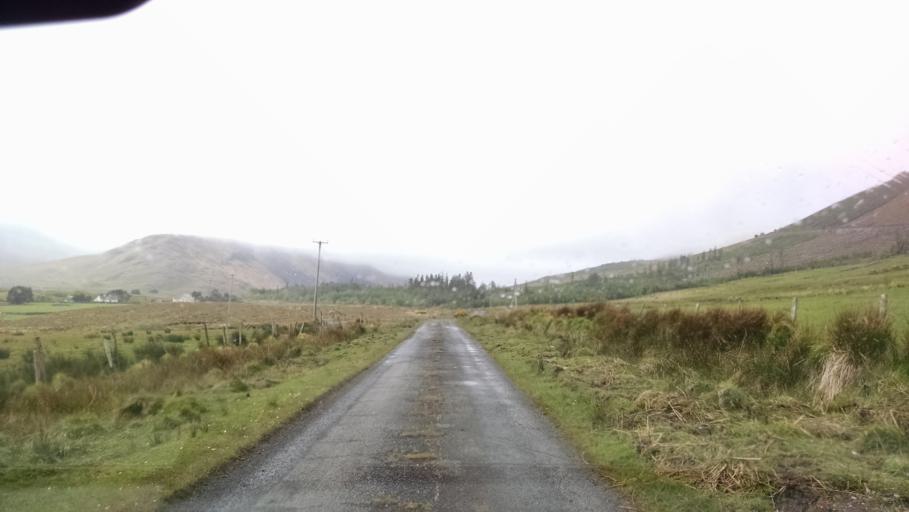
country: IE
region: Connaught
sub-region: Maigh Eo
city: Westport
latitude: 53.6477
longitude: -9.6575
